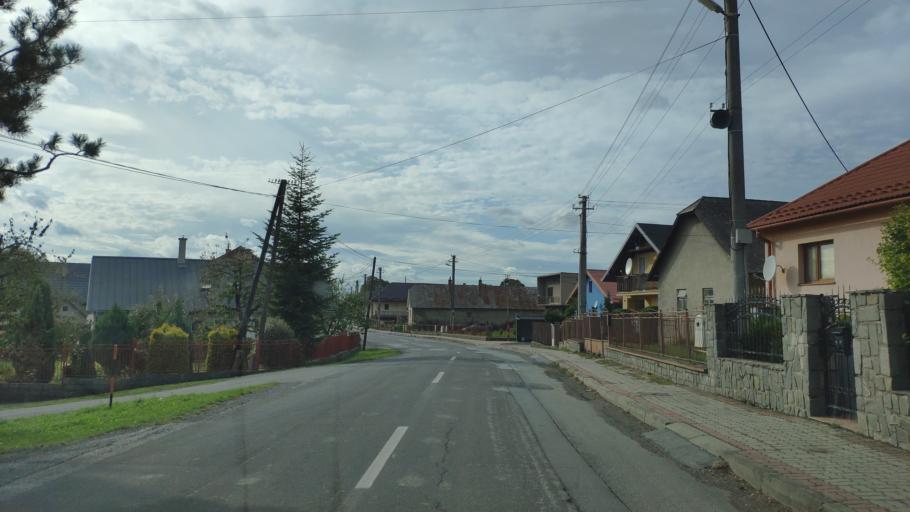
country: SK
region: Presovsky
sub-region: Okres Presov
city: Presov
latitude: 48.9458
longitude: 21.3396
